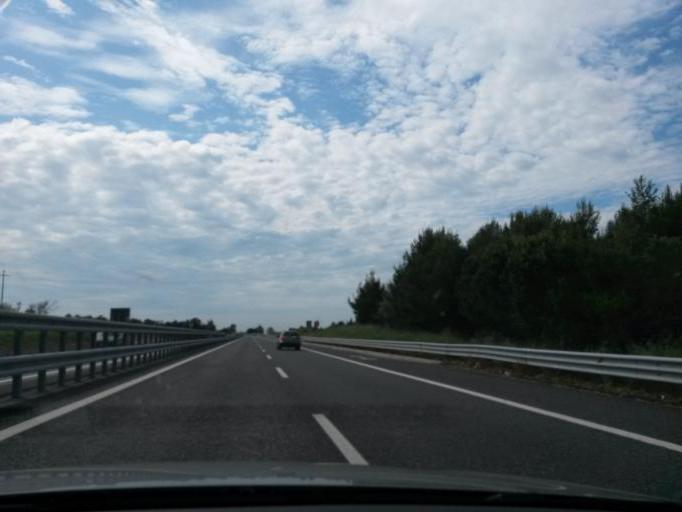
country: IT
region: Tuscany
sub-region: Provincia di Livorno
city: S.P. in Palazzi
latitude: 43.3542
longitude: 10.5139
